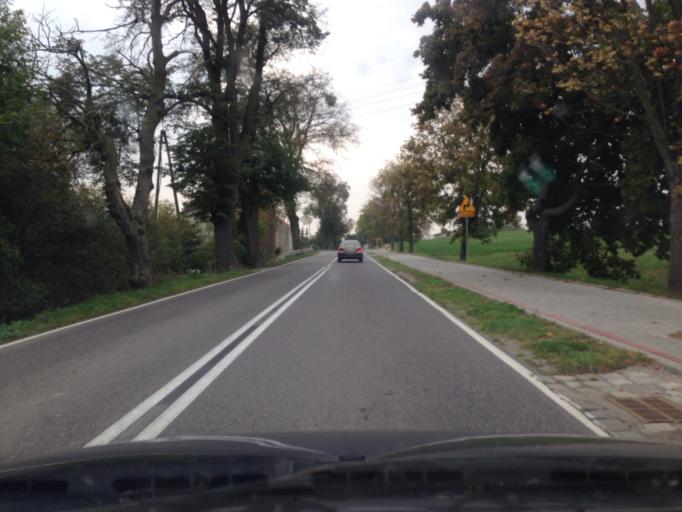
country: PL
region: Pomeranian Voivodeship
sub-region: Powiat kwidzynski
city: Kwidzyn
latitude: 53.7733
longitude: 18.9514
